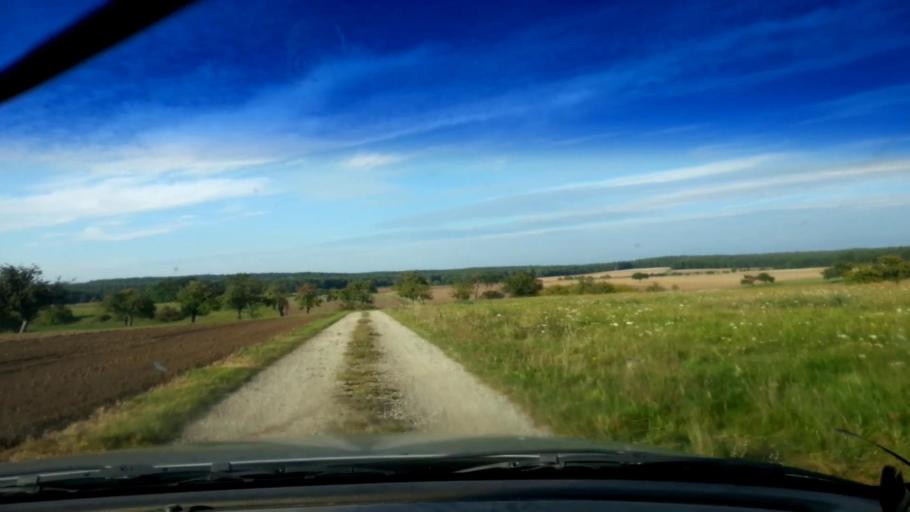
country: DE
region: Bavaria
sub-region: Upper Franconia
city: Viereth-Trunstadt
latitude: 49.9455
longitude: 10.7671
